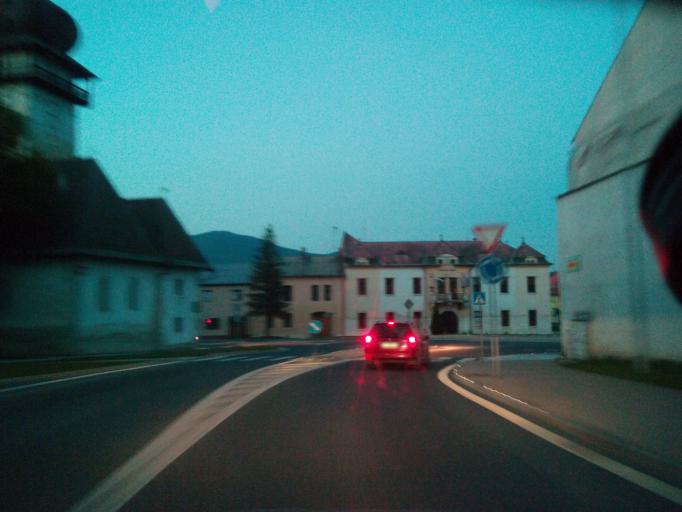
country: SK
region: Presovsky
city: Spisske Podhradie
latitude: 48.9487
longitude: 20.7935
